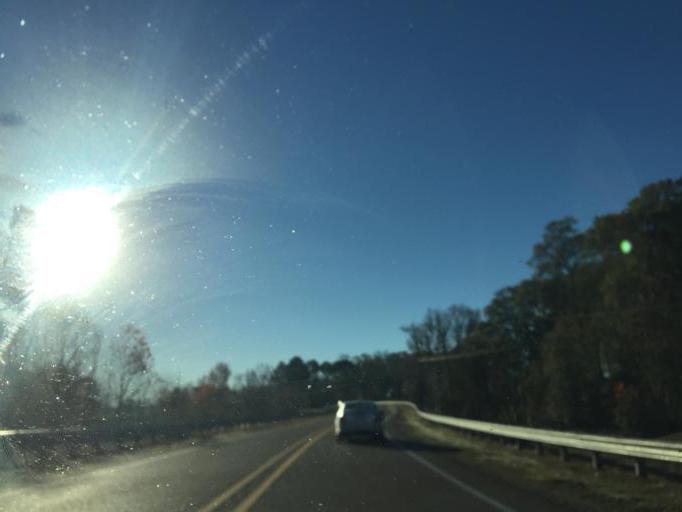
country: US
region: Mississippi
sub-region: Hinds County
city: Jackson
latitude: 32.2867
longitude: -90.1749
